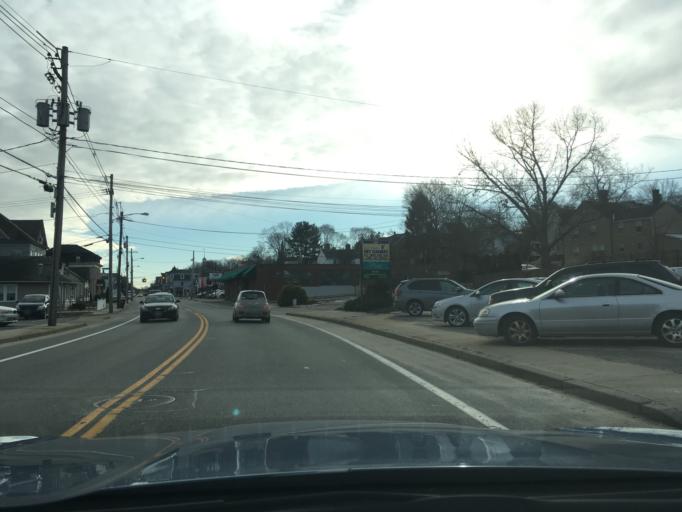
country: US
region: Rhode Island
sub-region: Kent County
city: East Greenwich
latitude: 41.6657
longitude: -71.4502
